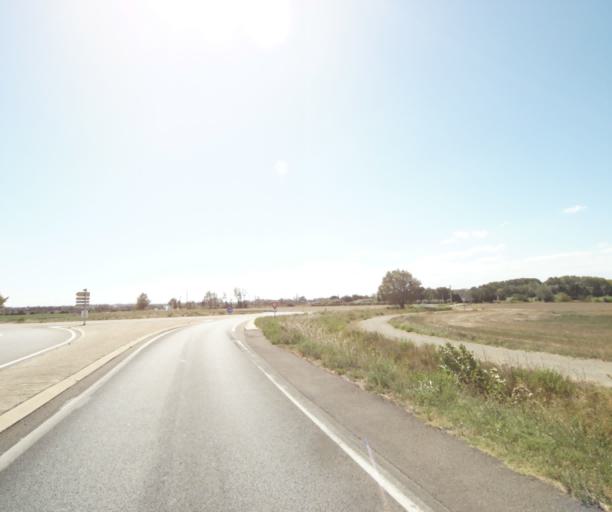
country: FR
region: Languedoc-Roussillon
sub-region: Departement du Gard
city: Rodilhan
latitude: 43.8256
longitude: 4.4199
